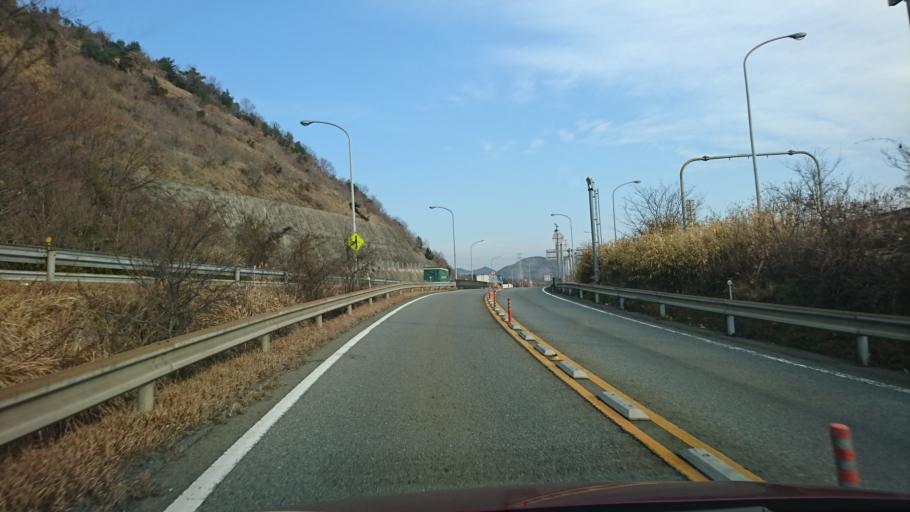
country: JP
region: Hyogo
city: Shirahamacho-usazakiminami
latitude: 34.8009
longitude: 134.7431
